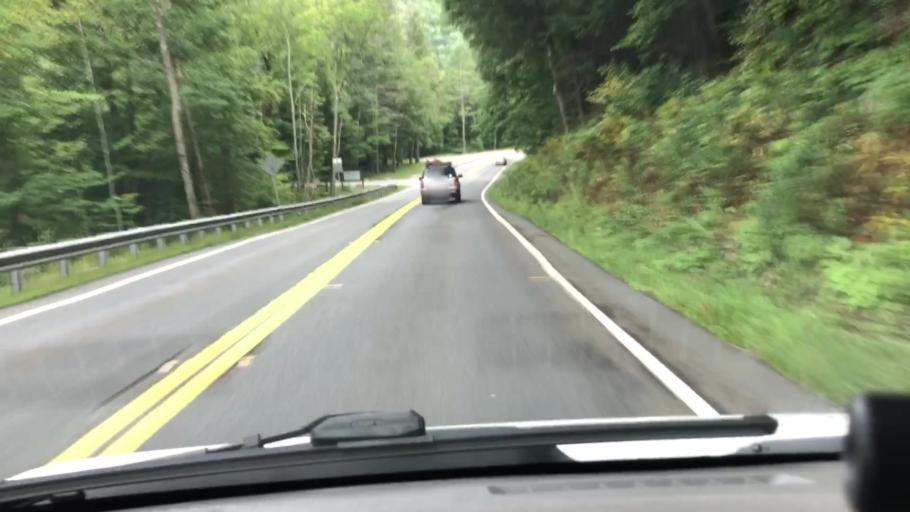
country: US
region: Massachusetts
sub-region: Franklin County
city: Charlemont
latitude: 42.6370
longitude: -72.9366
